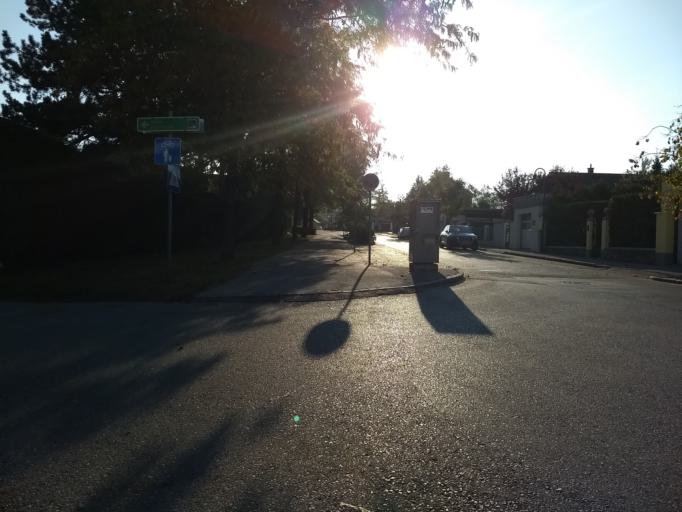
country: AT
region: Lower Austria
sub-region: Politischer Bezirk Modling
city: Perchtoldsdorf
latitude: 48.1210
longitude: 16.2736
